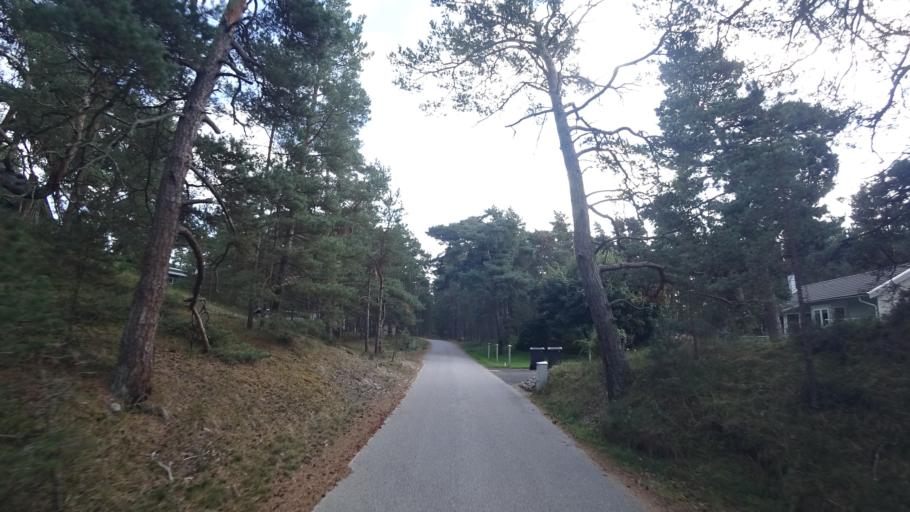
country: SE
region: Skane
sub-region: Kristianstads Kommun
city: Ahus
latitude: 55.9127
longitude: 14.2920
